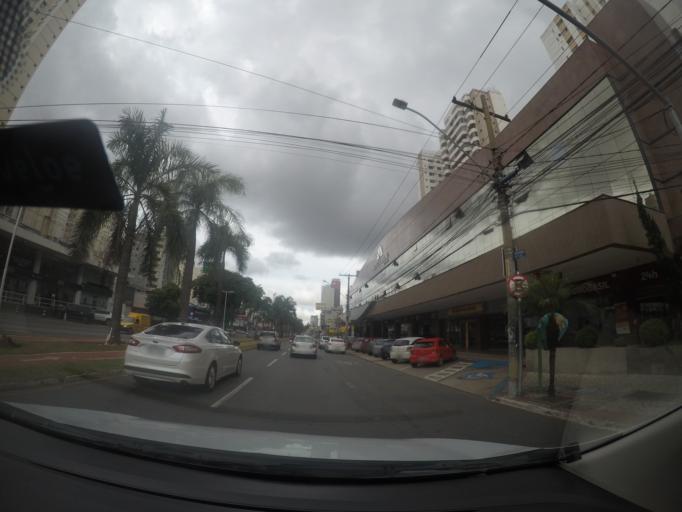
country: BR
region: Goias
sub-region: Goiania
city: Goiania
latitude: -16.7140
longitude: -49.2671
